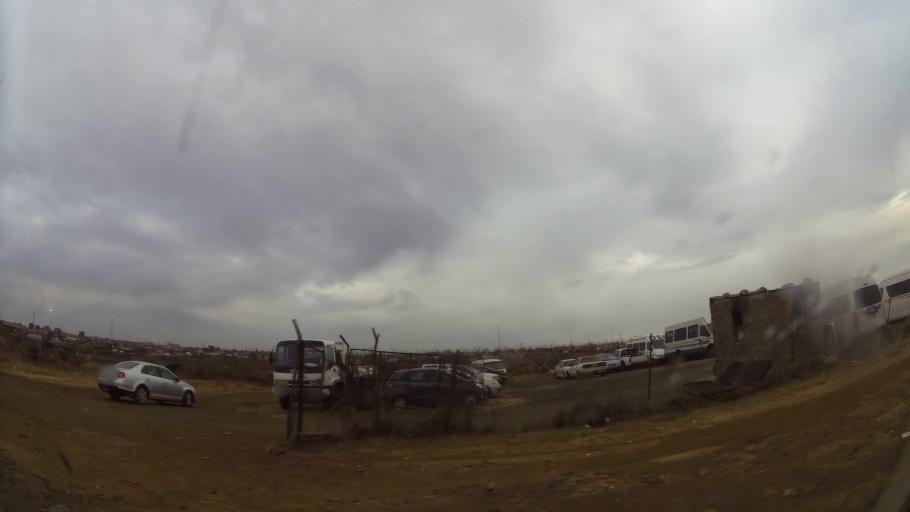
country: ZA
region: Gauteng
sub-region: Ekurhuleni Metropolitan Municipality
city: Germiston
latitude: -26.3759
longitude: 28.1734
